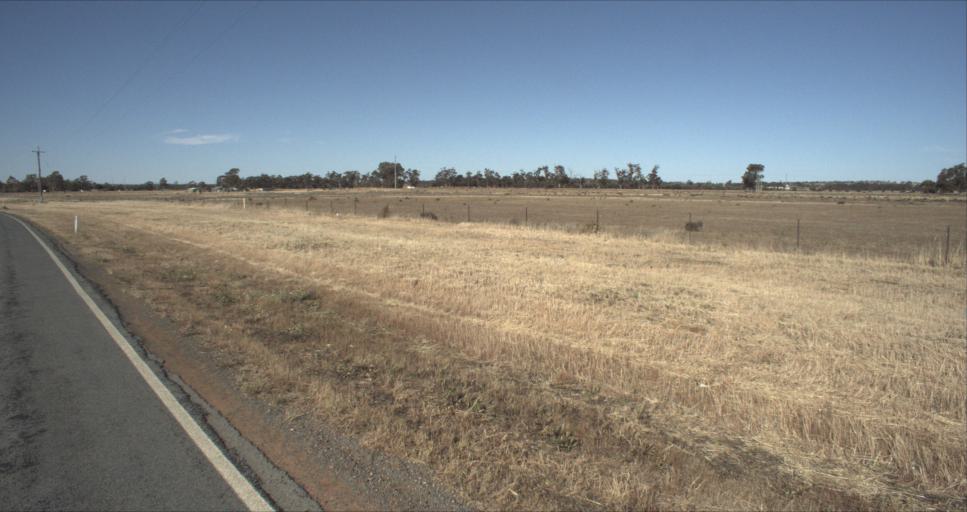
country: AU
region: New South Wales
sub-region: Leeton
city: Leeton
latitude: -34.6140
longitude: 146.4024
